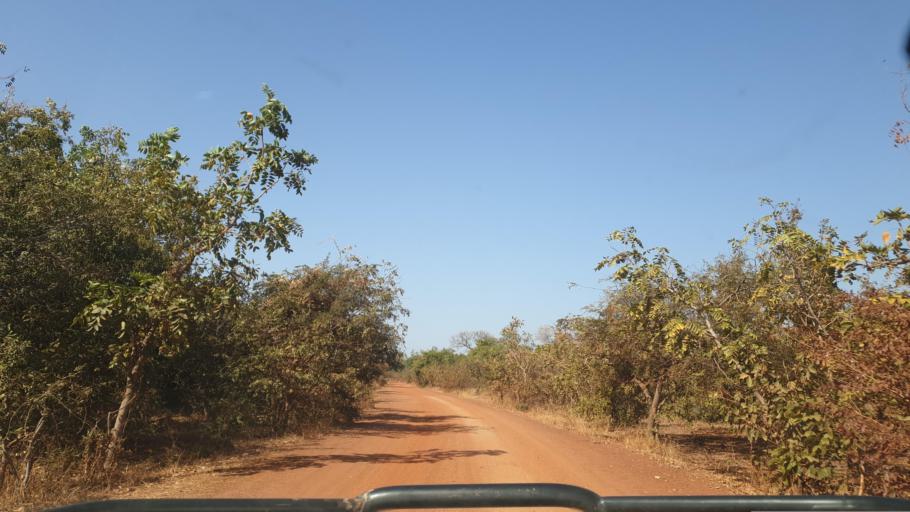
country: ML
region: Sikasso
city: Bougouni
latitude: 11.8207
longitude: -6.9518
